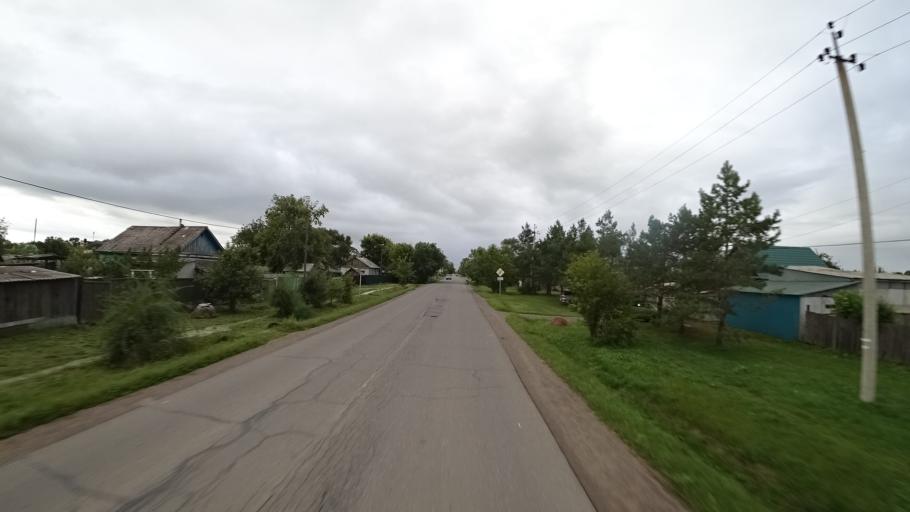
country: RU
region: Primorskiy
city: Chernigovka
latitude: 44.3378
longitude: 132.5880
